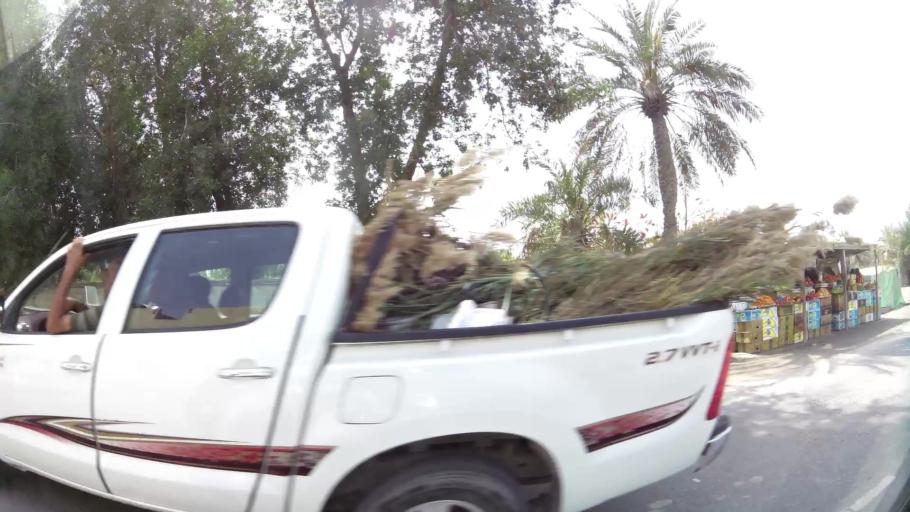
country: BH
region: Manama
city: Jidd Hafs
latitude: 26.2306
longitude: 50.4912
